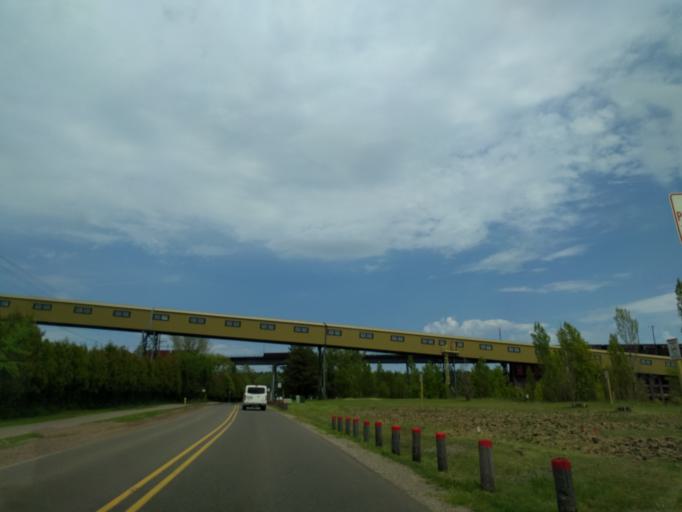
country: US
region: Michigan
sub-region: Marquette County
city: Marquette
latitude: 46.5790
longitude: -87.3917
